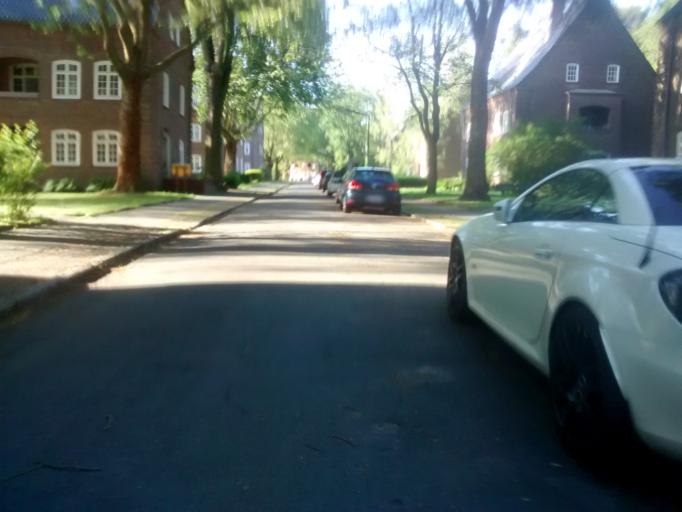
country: DE
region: Brandenburg
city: Hohen Neuendorf
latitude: 52.6575
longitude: 13.2850
